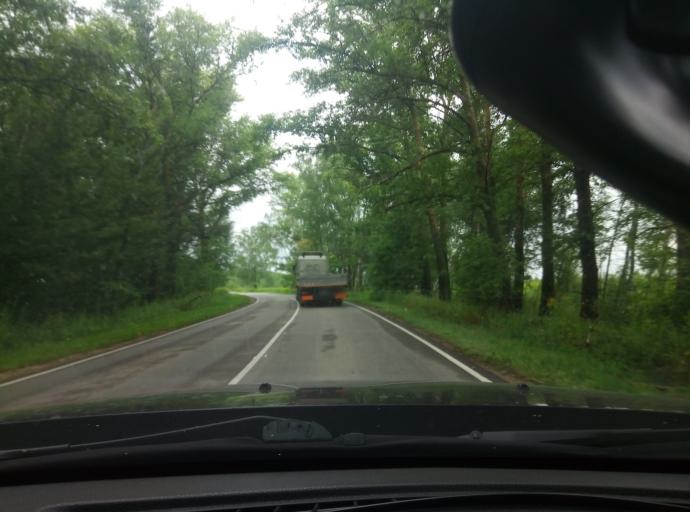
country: RU
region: Tula
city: Lomintsevskiy
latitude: 53.9640
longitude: 37.7148
